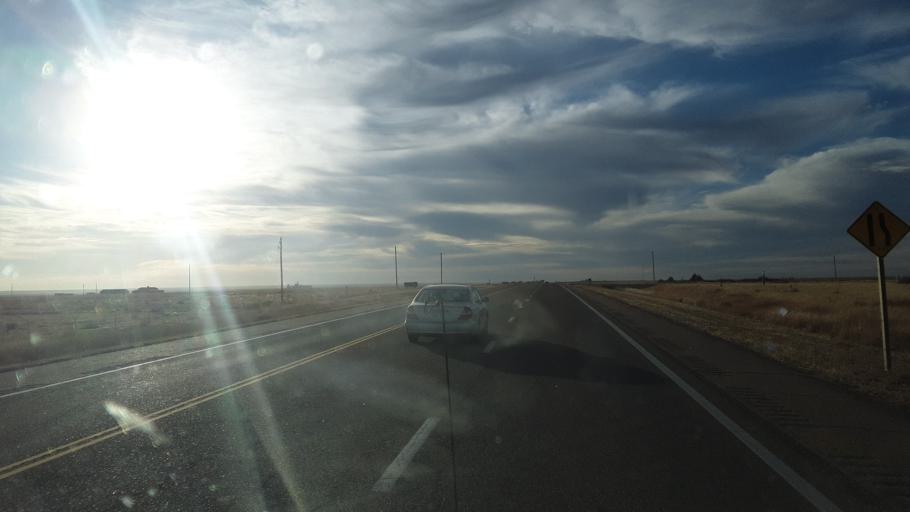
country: US
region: Kansas
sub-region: Hamilton County
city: Syracuse
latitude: 37.9440
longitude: -101.5119
